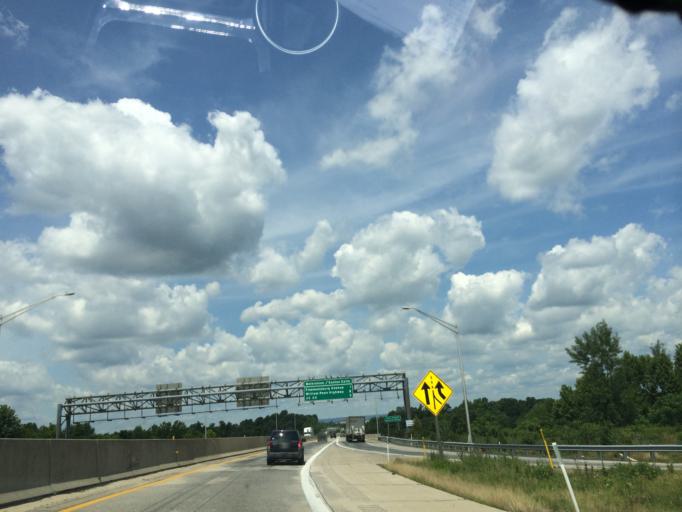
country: US
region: Pennsylvania
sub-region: Northampton County
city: Old Orchard
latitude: 40.6394
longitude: -75.2739
